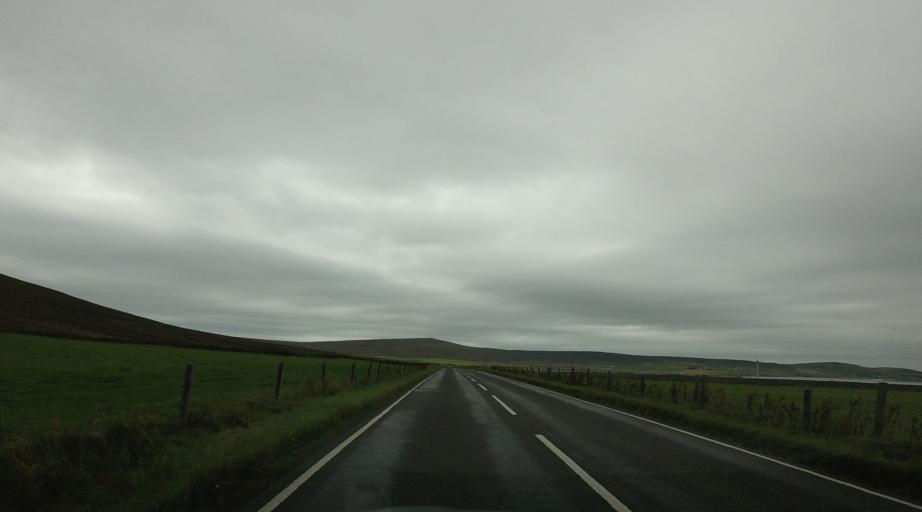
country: GB
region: Scotland
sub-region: Orkney Islands
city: Orkney
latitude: 59.0002
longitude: -3.0267
